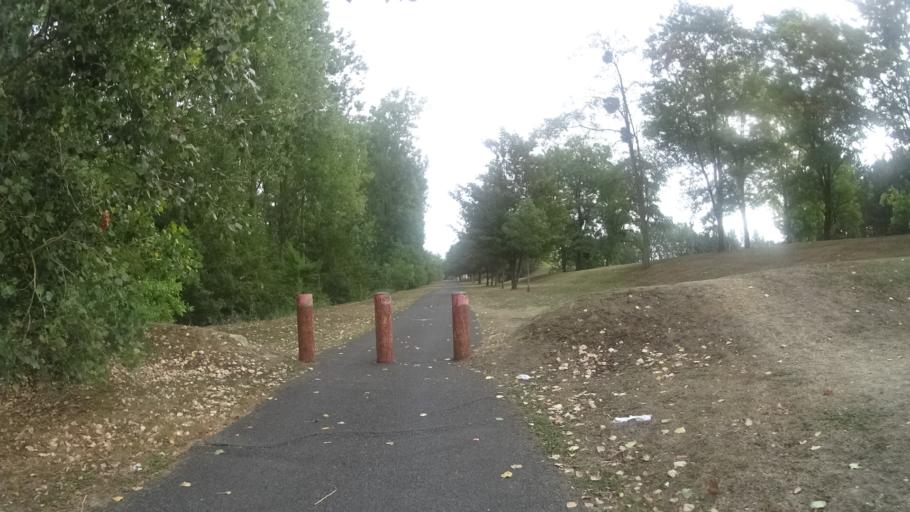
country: FR
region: Picardie
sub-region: Departement de l'Oise
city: Lacroix-Saint-Ouen
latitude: 49.3687
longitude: 2.7716
